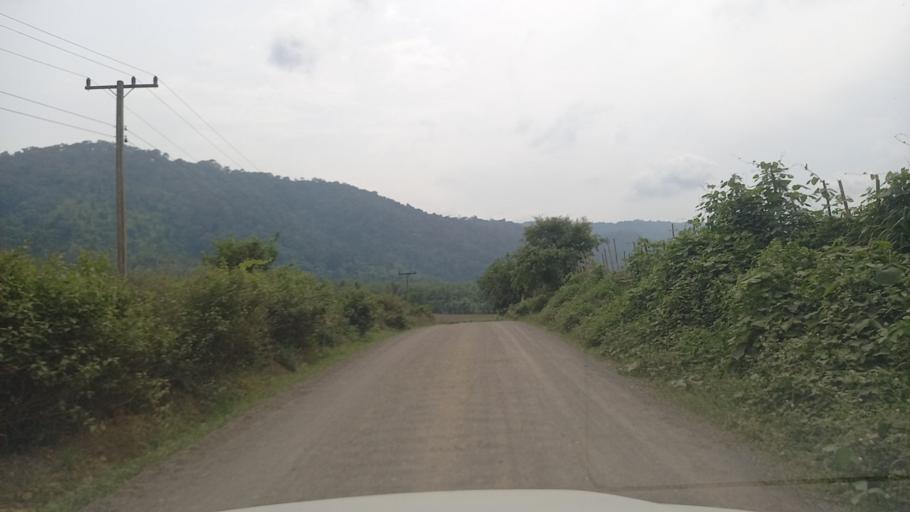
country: LA
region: Bolikhamxai
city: Ban Nahin
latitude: 18.1500
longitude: 104.7419
